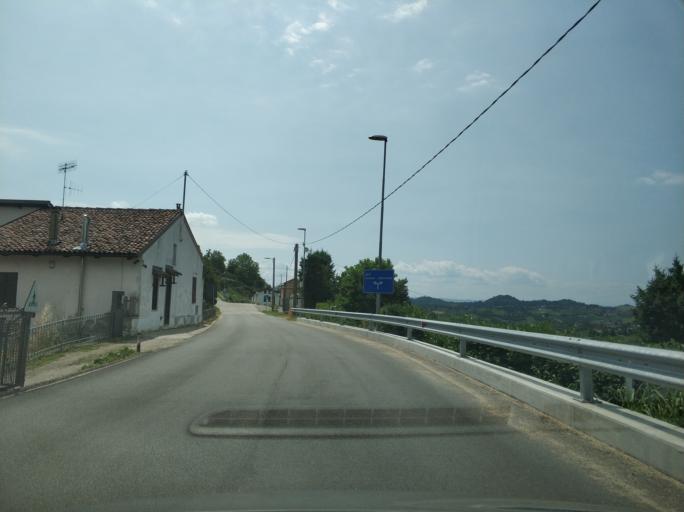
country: IT
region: Piedmont
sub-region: Provincia di Cuneo
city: Santo Stefano Roero
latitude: 44.7863
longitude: 7.9435
